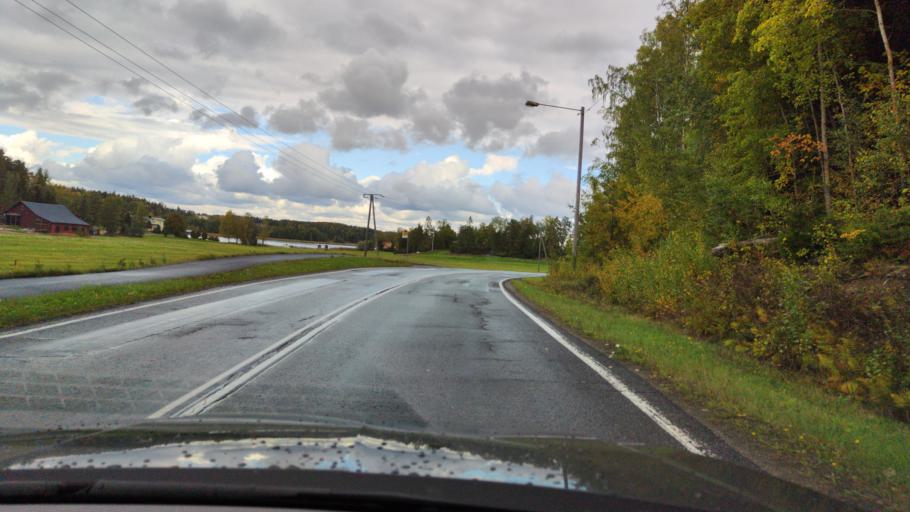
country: FI
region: Varsinais-Suomi
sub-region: Turku
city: Turku
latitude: 60.3635
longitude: 22.1950
